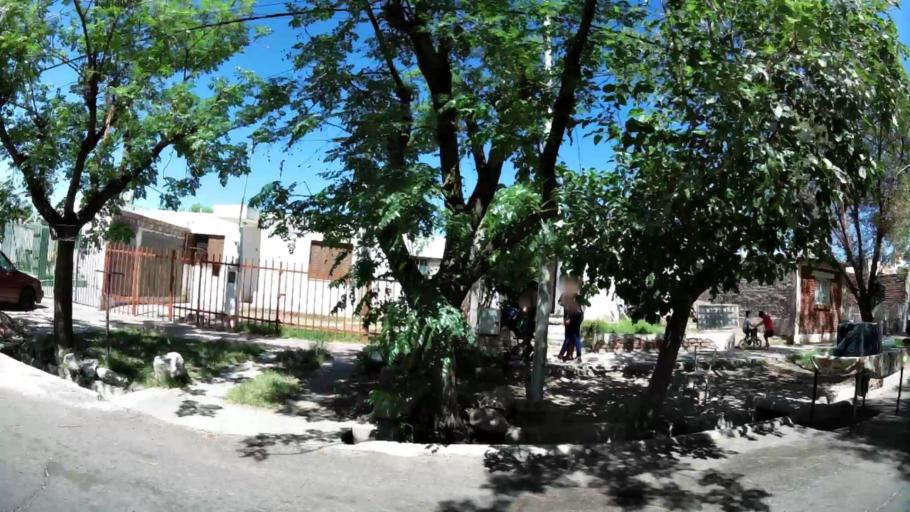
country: AR
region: Mendoza
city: Las Heras
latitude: -32.8413
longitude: -68.8668
